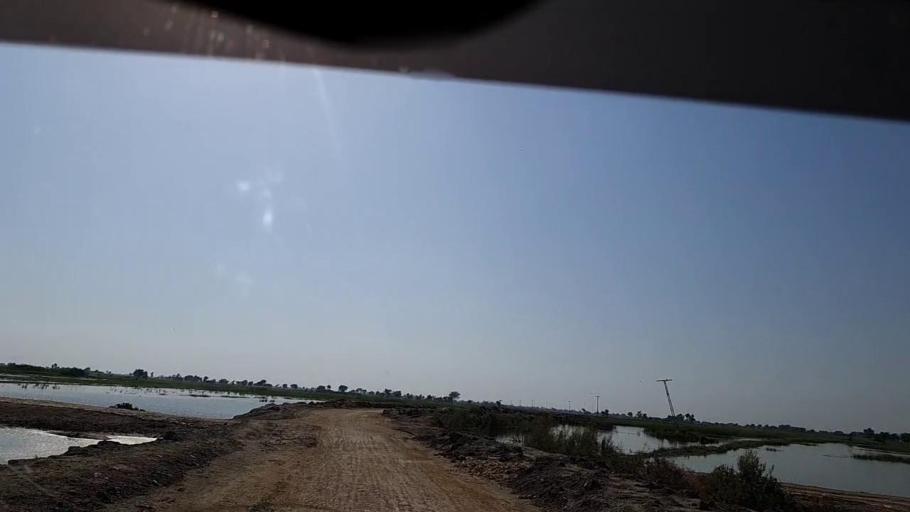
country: PK
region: Sindh
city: Tangwani
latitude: 28.3610
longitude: 69.0251
